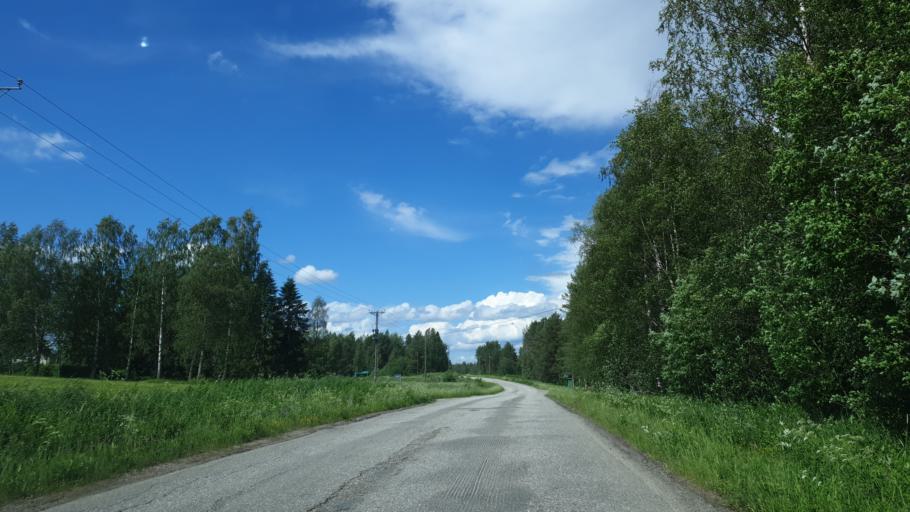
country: FI
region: Northern Savo
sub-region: Koillis-Savo
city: Kaavi
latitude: 62.9947
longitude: 28.7198
